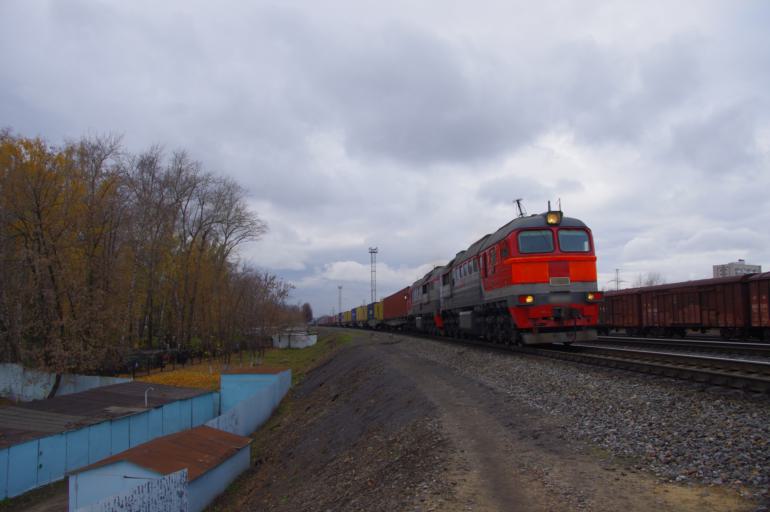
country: RU
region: Moscow
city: Leonovo
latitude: 55.8446
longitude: 37.6491
